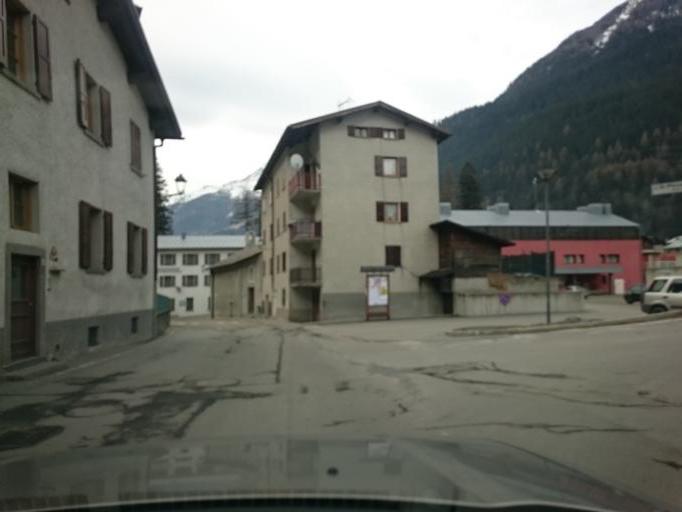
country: IT
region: Lombardy
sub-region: Provincia di Sondrio
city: Valdisotto
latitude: 46.4285
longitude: 10.3560
